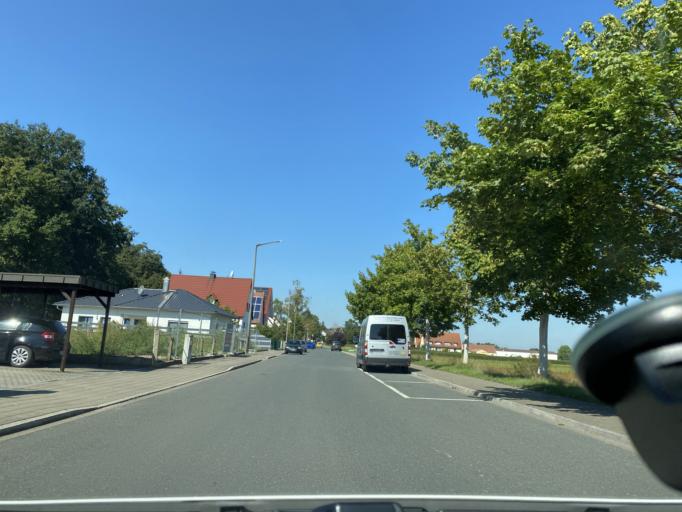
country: DE
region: Bavaria
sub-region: Regierungsbezirk Mittelfranken
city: Furth
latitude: 49.4983
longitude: 11.0028
